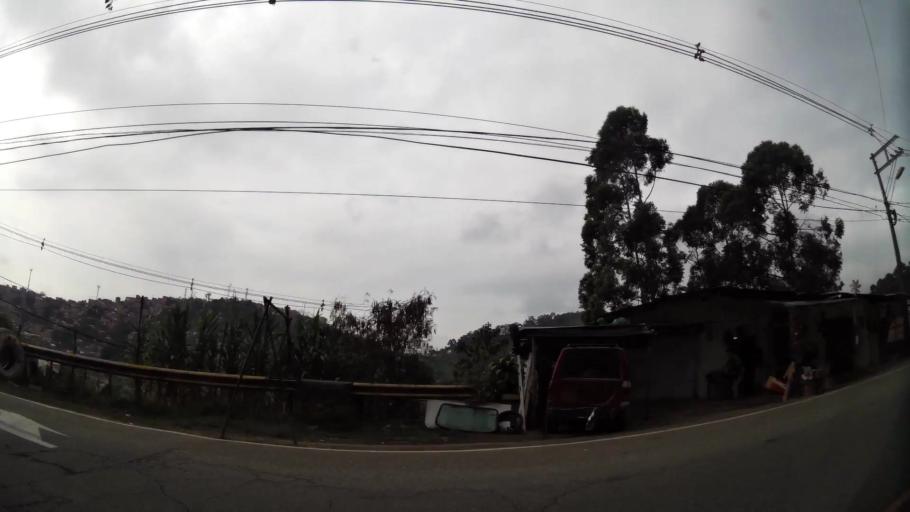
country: CO
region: Antioquia
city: Medellin
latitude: 6.2776
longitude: -75.6150
